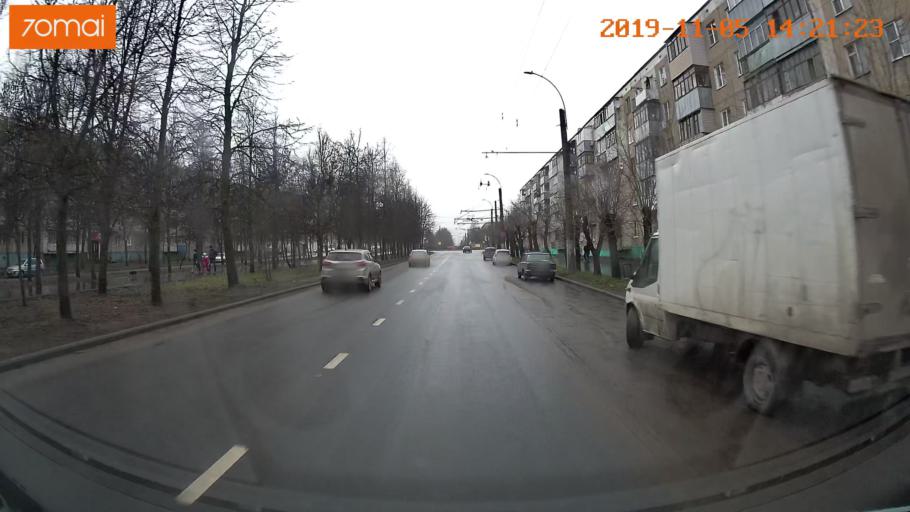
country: RU
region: Ivanovo
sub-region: Gorod Ivanovo
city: Ivanovo
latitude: 56.9591
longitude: 41.0111
